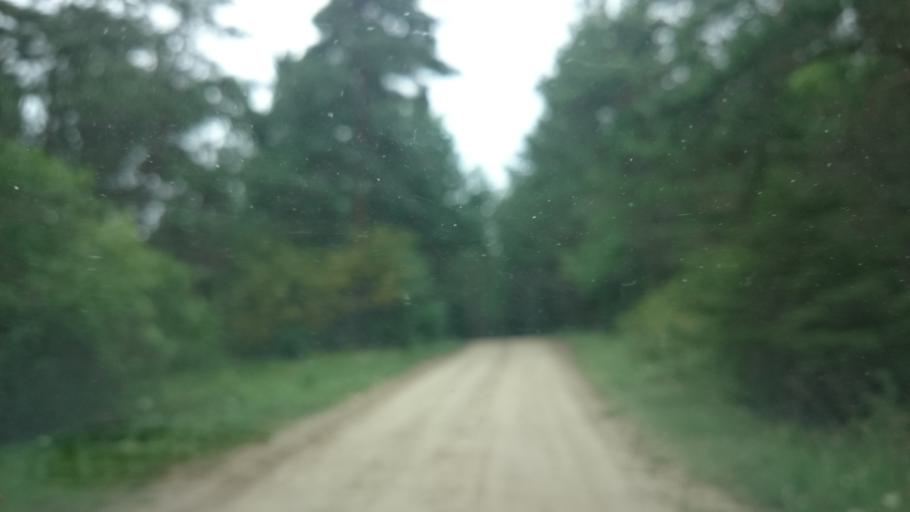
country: EE
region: Saare
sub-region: Orissaare vald
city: Orissaare
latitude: 58.5887
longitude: 22.7051
